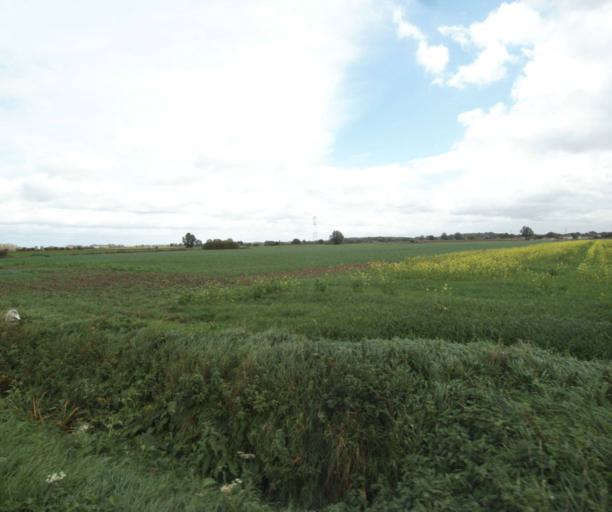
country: FR
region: Nord-Pas-de-Calais
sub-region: Departement du Nord
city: Houplines
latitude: 50.6693
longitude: 2.9268
